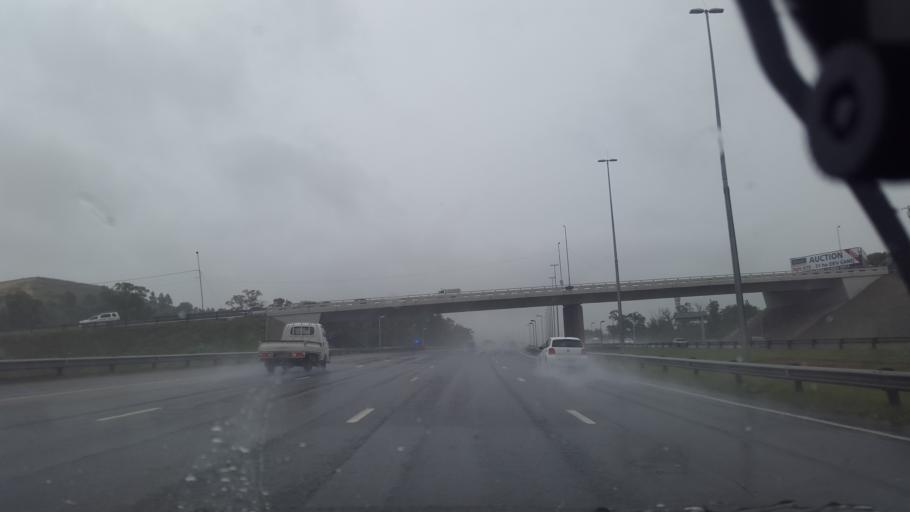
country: ZA
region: Gauteng
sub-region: City of Johannesburg Metropolitan Municipality
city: Johannesburg
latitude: -26.2326
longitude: 27.9604
